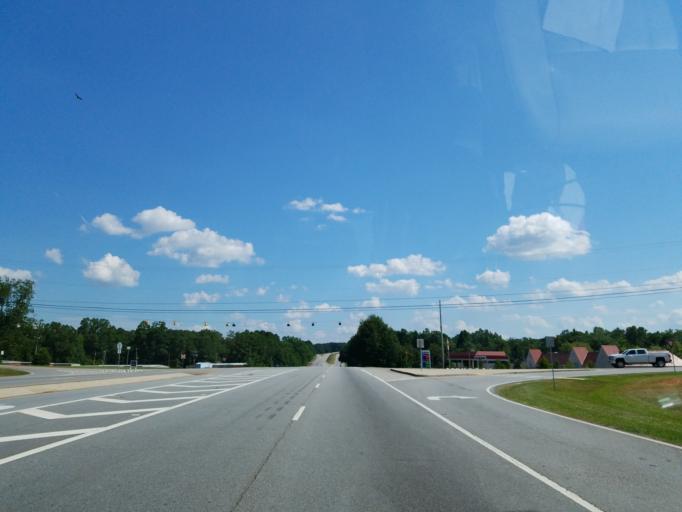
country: US
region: Georgia
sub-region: Lamar County
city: Barnesville
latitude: 33.0646
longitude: -84.1692
